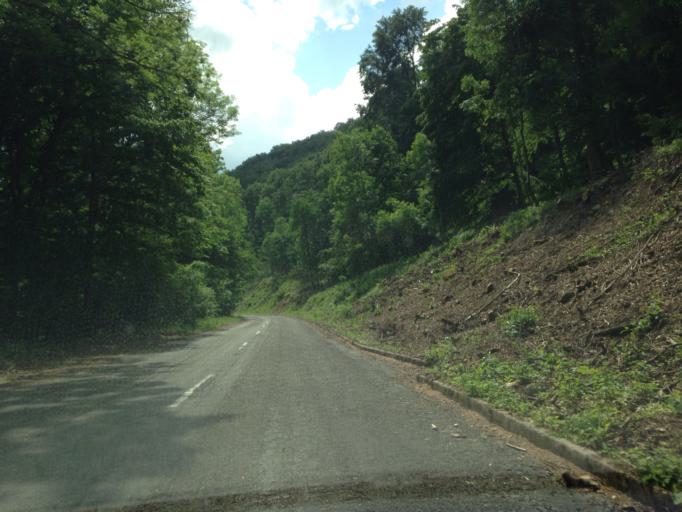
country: HU
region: Pest
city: Visegrad
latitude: 47.7503
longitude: 18.9424
